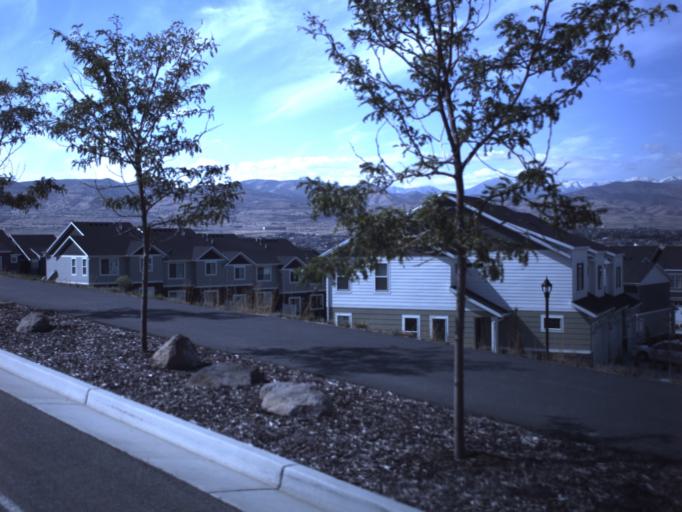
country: US
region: Utah
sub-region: Salt Lake County
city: Bluffdale
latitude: 40.4785
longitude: -111.9090
